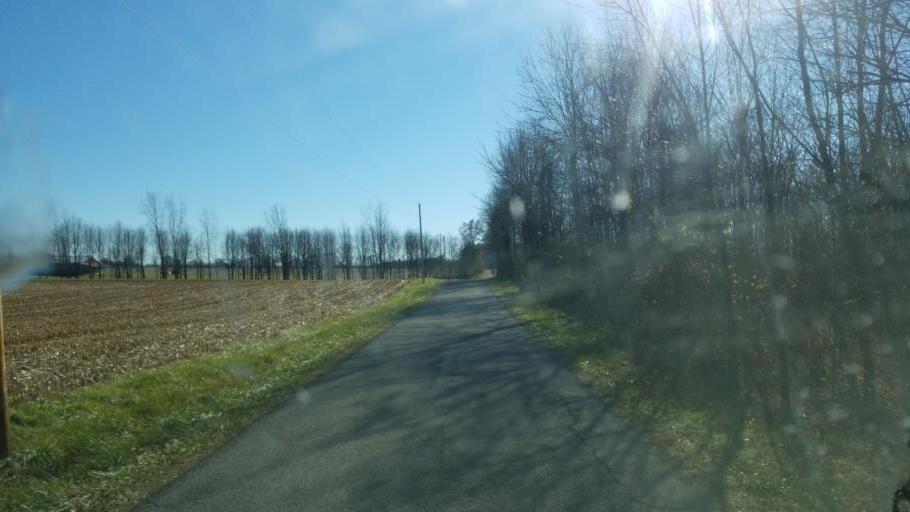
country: US
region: Ohio
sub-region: Crawford County
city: Galion
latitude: 40.7356
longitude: -82.8393
